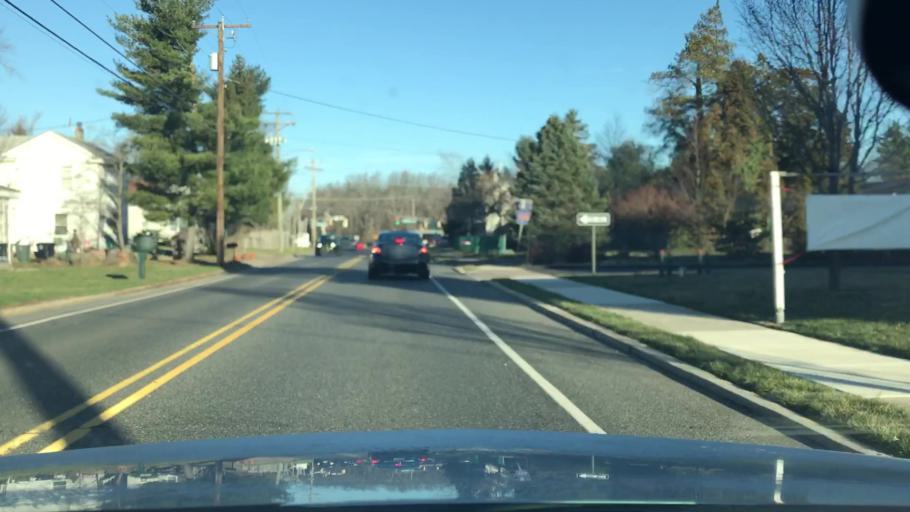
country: US
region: New Jersey
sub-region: Gloucester County
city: Williamstown
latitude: 39.7122
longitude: -75.0285
